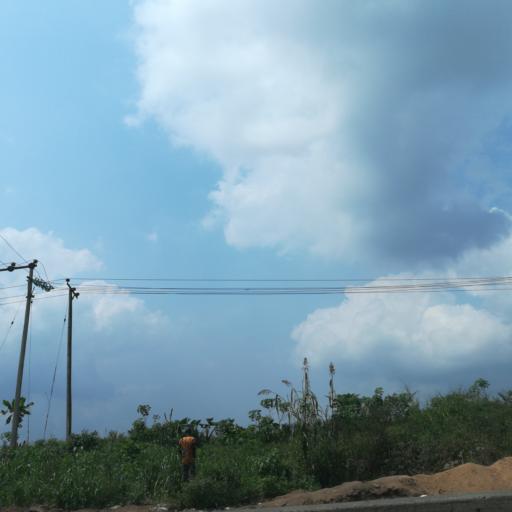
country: NG
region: Rivers
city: Okrika
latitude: 4.8102
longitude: 7.0990
